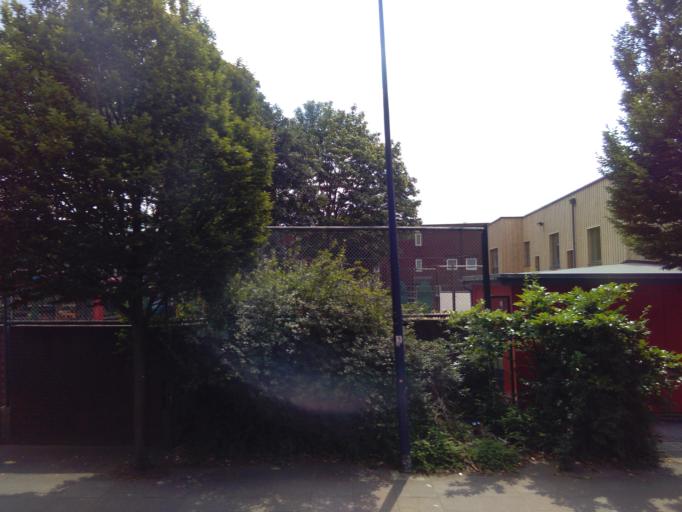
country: GB
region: England
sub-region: Greater London
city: Catford
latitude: 51.4734
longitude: -0.0509
